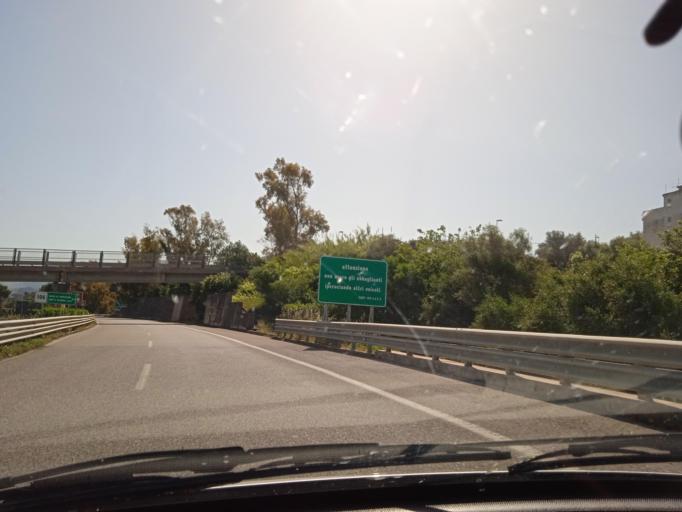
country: IT
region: Sicily
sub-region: Messina
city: Sant'Agata di Militello
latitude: 38.0605
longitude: 14.6335
